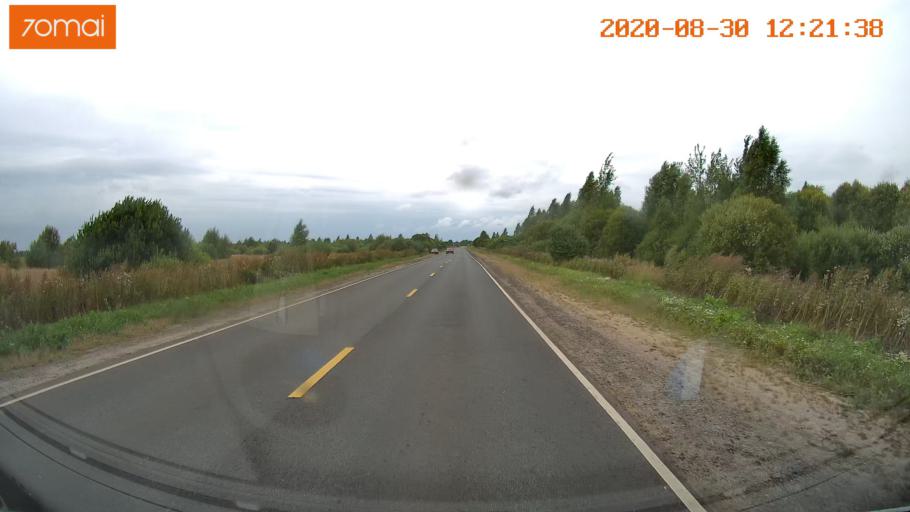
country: RU
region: Ivanovo
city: Yur'yevets
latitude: 57.3261
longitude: 42.8706
